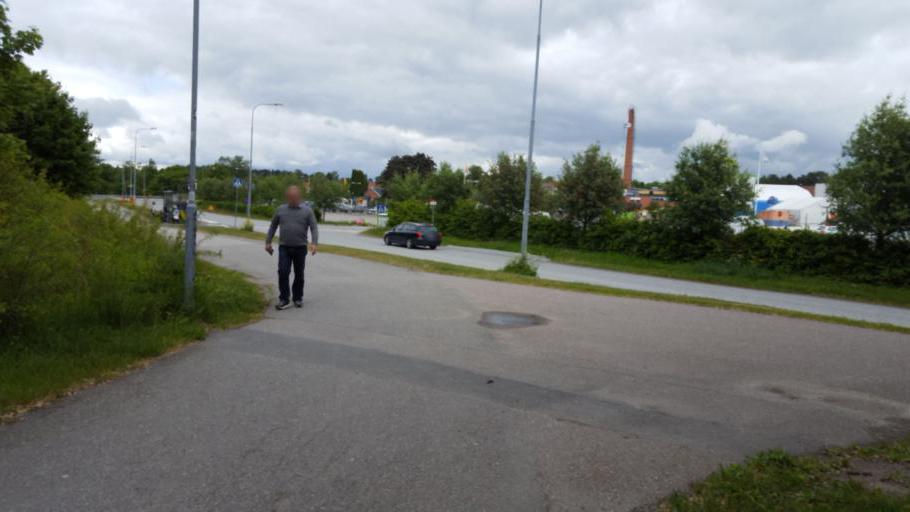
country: SE
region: Stockholm
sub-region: Upplands Vasby Kommun
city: Upplands Vaesby
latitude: 59.5139
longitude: 17.8869
